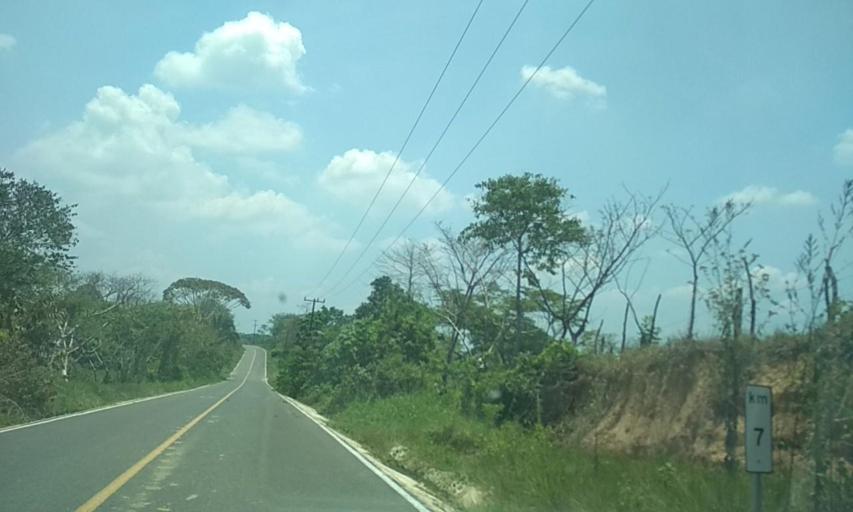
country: MX
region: Tabasco
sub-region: Huimanguillo
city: Francisco Rueda
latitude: 17.7609
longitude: -94.0577
